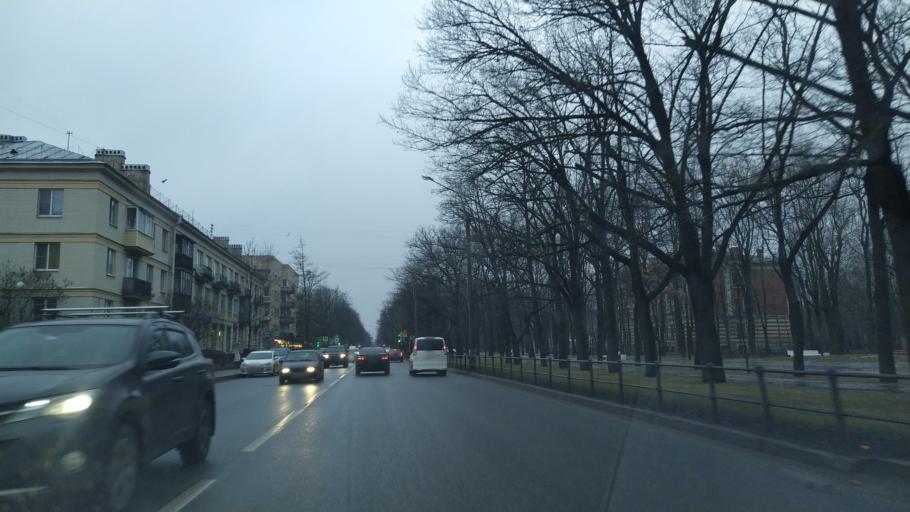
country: RU
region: St.-Petersburg
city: Pushkin
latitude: 59.7222
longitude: 30.4153
